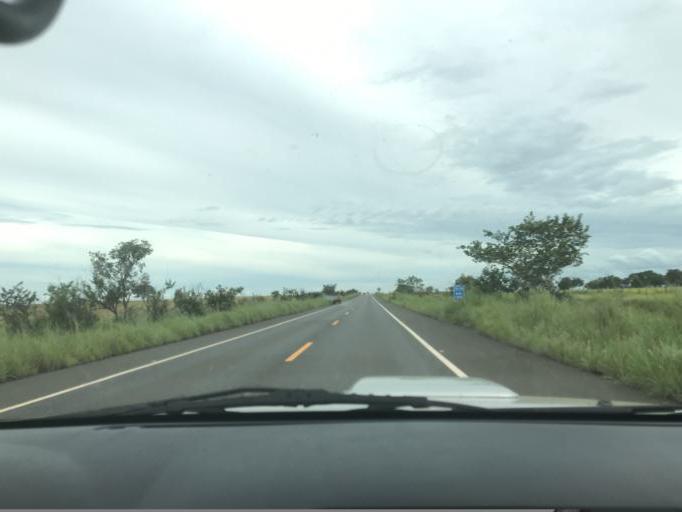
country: BR
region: Minas Gerais
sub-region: Araxa
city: Araxa
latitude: -19.3878
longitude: -46.8586
